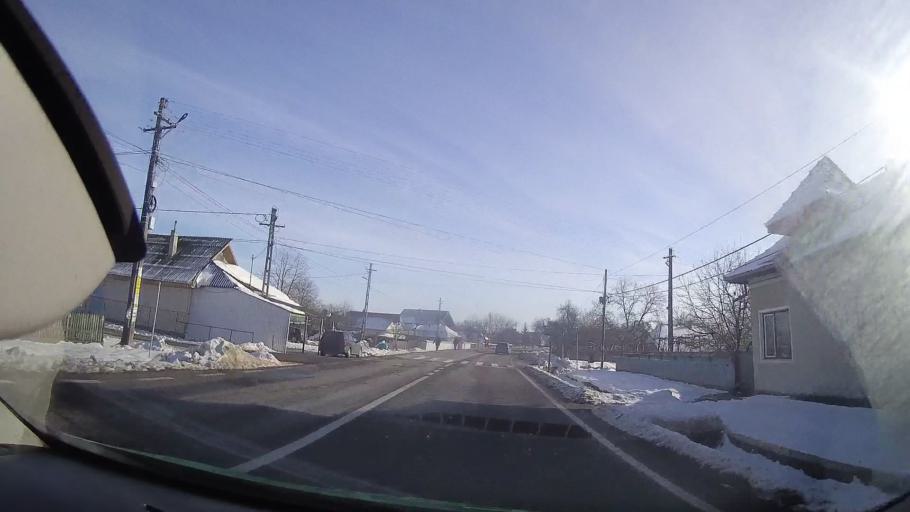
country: RO
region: Neamt
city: Bodesti
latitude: 47.0528
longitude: 26.4007
